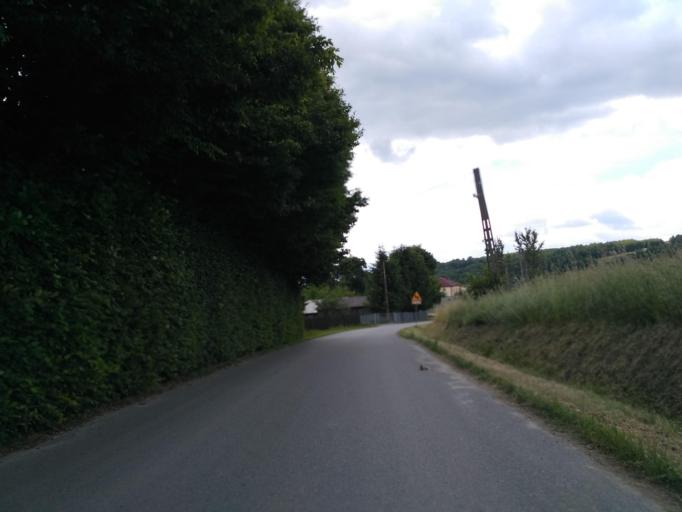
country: PL
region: Subcarpathian Voivodeship
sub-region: Powiat przeworski
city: Jawornik Polski
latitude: 49.8582
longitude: 22.2876
